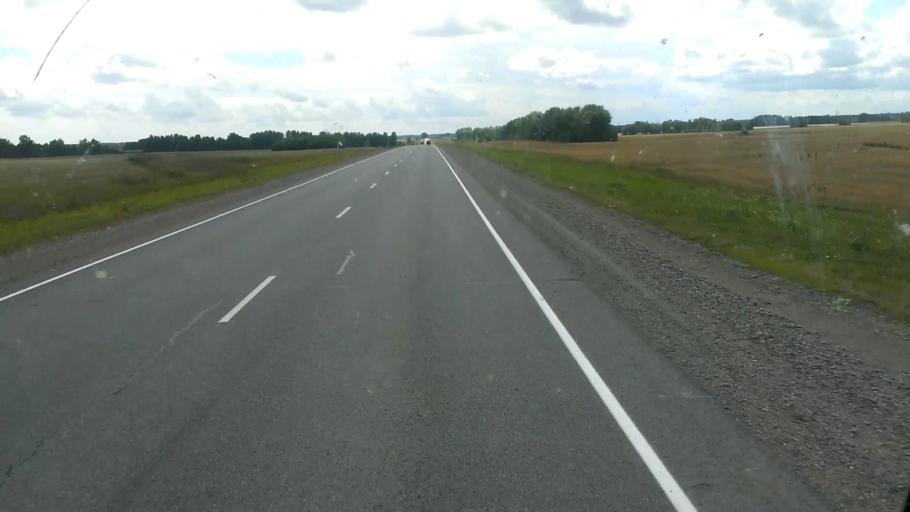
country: RU
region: Altai Krai
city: Troitskoye
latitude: 52.8961
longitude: 84.8345
